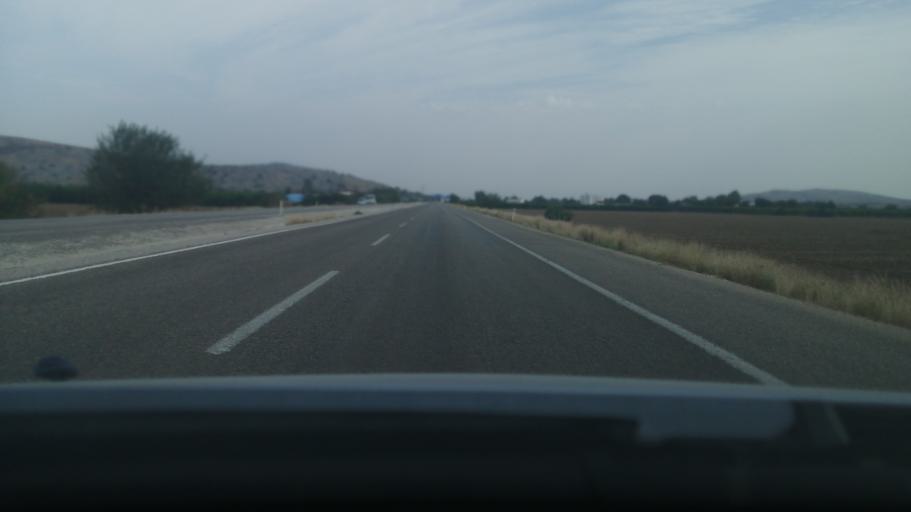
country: TR
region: Adana
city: Kozan
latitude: 37.3831
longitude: 35.8150
